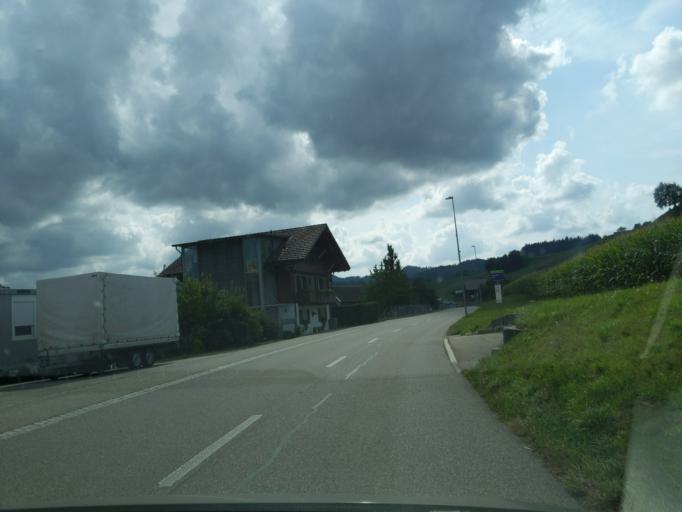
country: CH
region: Bern
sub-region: Oberaargau
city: Wyssachen
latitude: 47.0917
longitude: 7.8263
